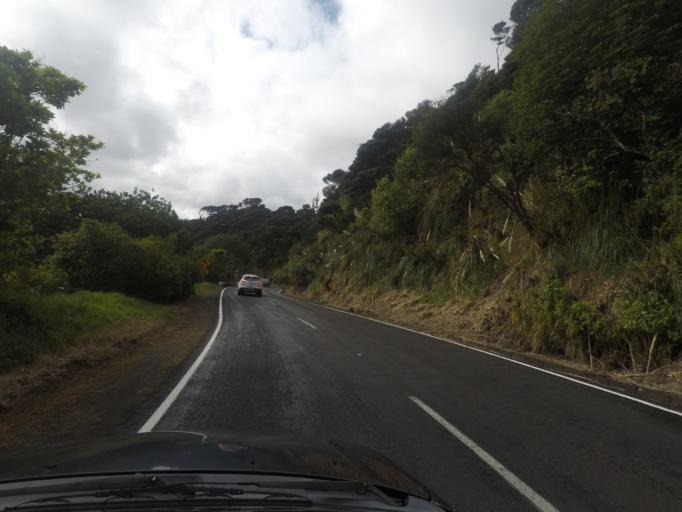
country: NZ
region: Auckland
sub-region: Auckland
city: Titirangi
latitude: -37.0049
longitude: 174.5790
